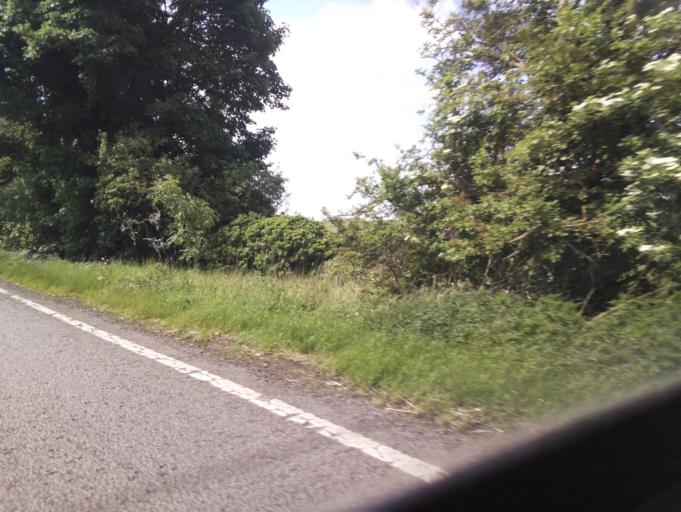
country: GB
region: England
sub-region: Lincolnshire
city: Burton
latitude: 53.3492
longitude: -0.5447
